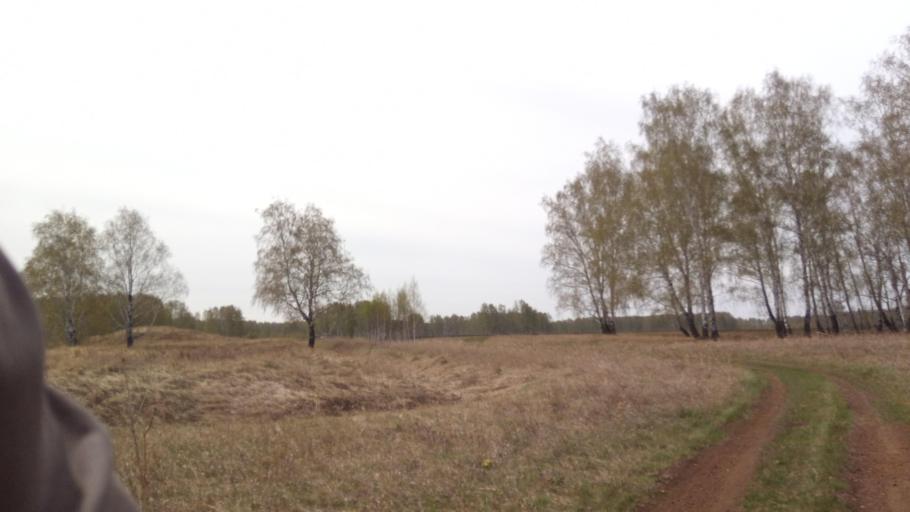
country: RU
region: Chelyabinsk
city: Timiryazevskiy
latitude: 55.0125
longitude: 60.8593
